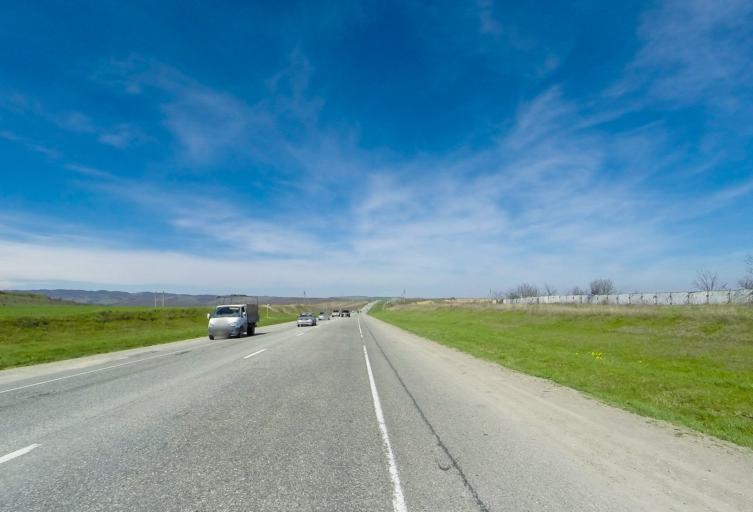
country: RU
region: Kabardino-Balkariya
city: Dugulubgey
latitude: 43.6450
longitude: 43.5322
